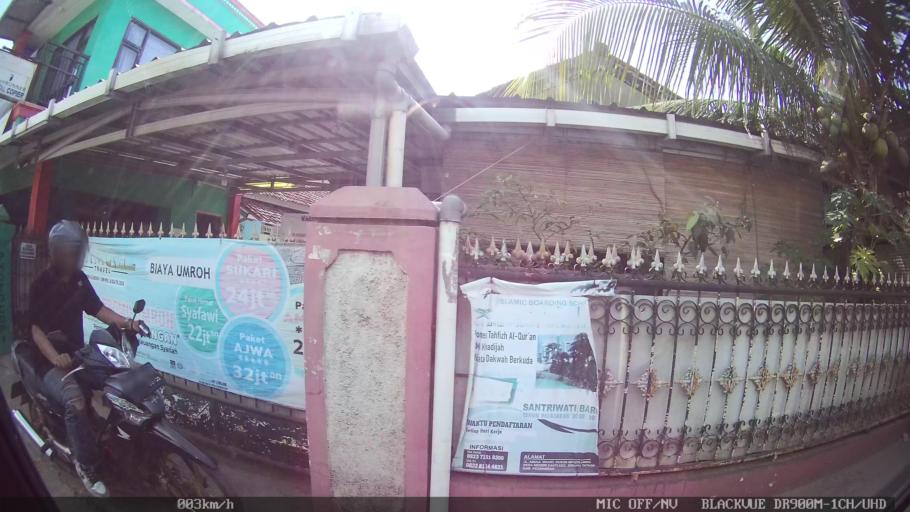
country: ID
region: Lampung
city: Kedaton
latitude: -5.3733
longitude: 105.2386
